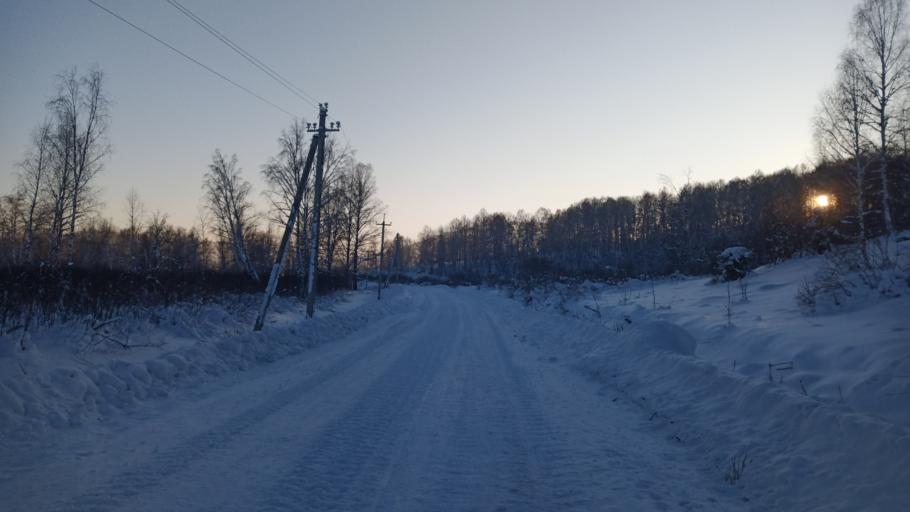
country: RU
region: Altai Krai
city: Krasnogorskoye
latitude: 52.1265
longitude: 86.2048
